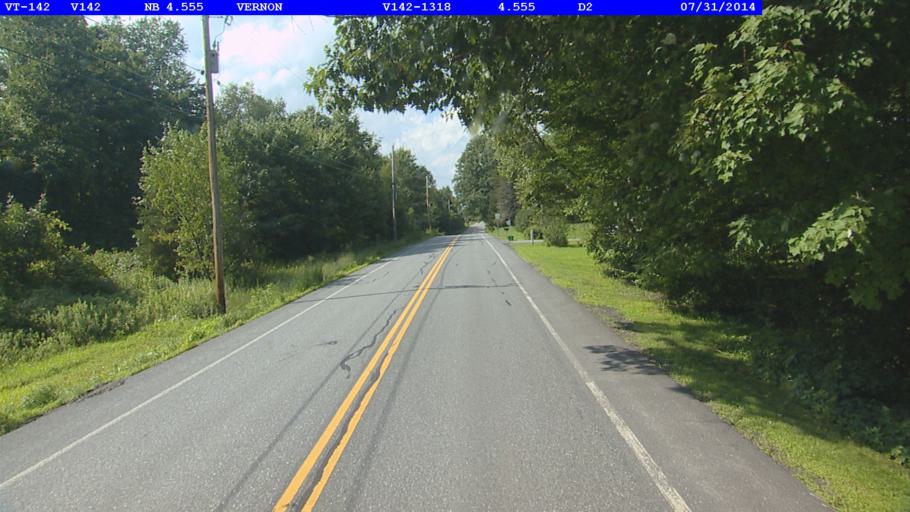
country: US
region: New Hampshire
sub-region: Cheshire County
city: Hinsdale
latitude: 42.7704
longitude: -72.5198
